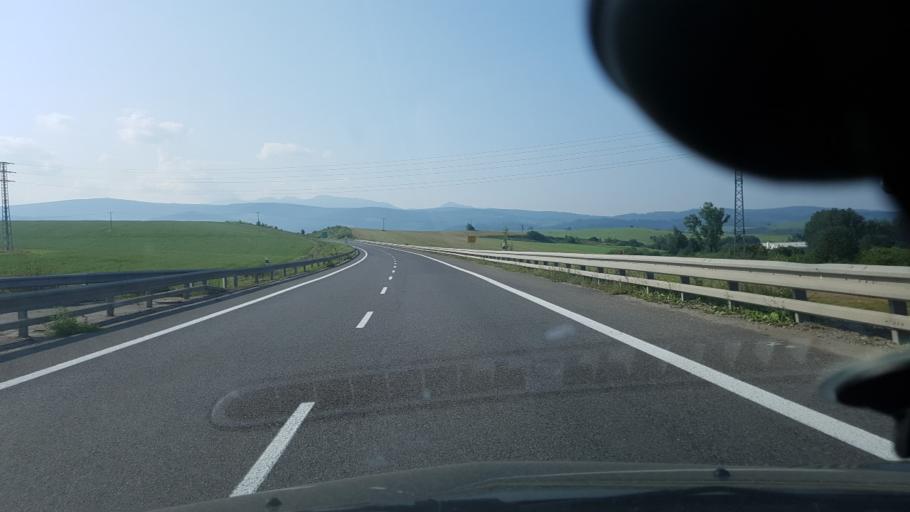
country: SK
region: Zilinsky
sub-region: Okres Zilina
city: Trstena
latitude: 49.3721
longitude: 19.6298
